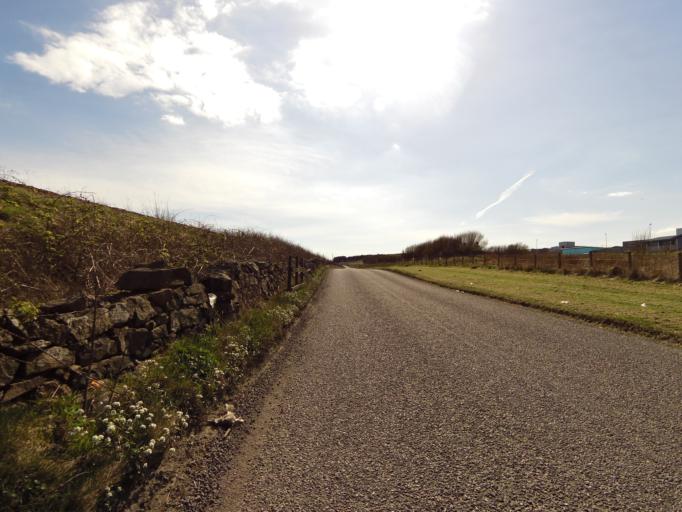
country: GB
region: Scotland
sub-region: Aberdeen City
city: Aberdeen
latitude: 57.1152
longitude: -2.0642
